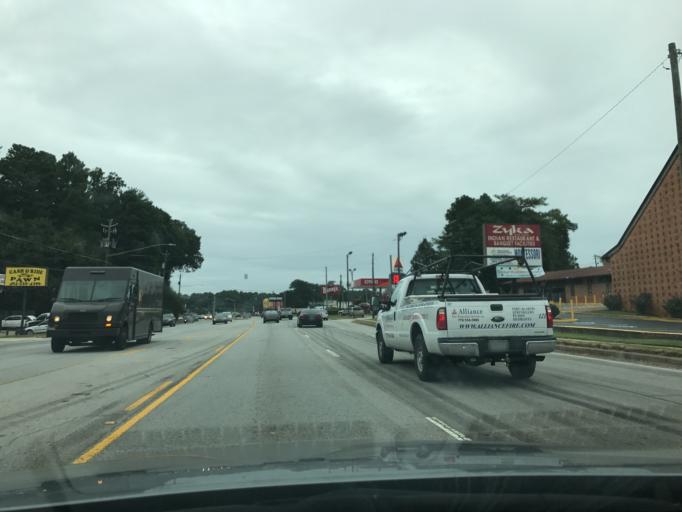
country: US
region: Georgia
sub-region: DeKalb County
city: Scottdale
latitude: 33.7968
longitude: -84.2845
